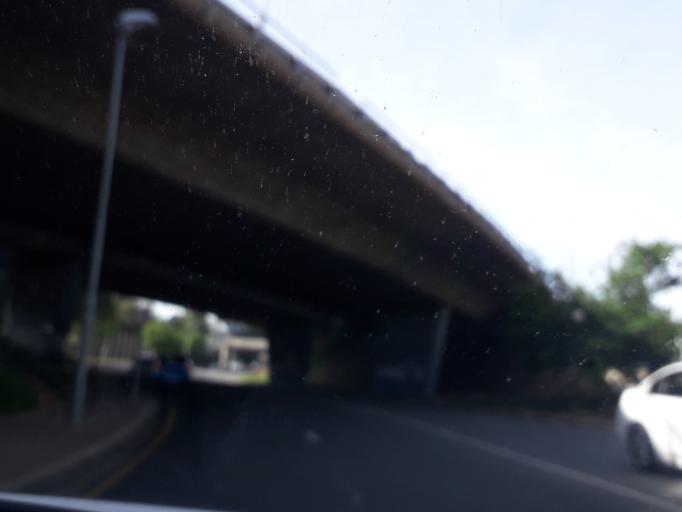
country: ZA
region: Gauteng
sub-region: City of Johannesburg Metropolitan Municipality
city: Johannesburg
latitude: -26.1857
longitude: 28.0276
